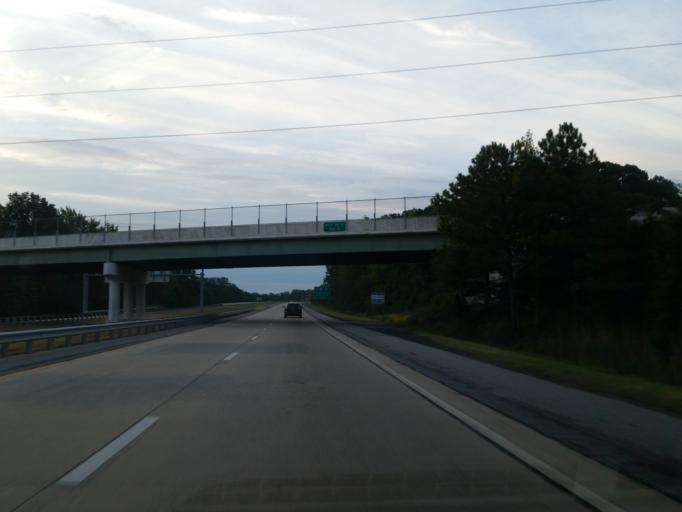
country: US
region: Delaware
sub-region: Kent County
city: Dover
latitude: 39.1770
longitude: -75.5032
